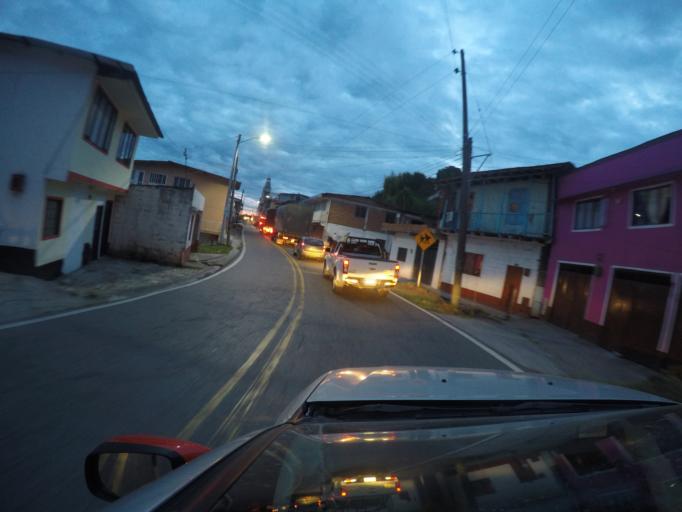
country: CO
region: Tolima
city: Herveo
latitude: 5.1340
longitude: -75.1444
